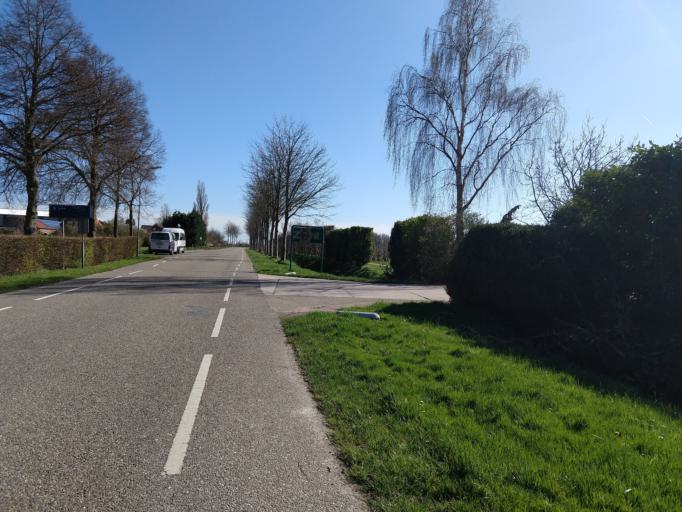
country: NL
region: Zeeland
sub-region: Gemeente Goes
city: Goes
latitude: 51.5215
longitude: 3.9466
